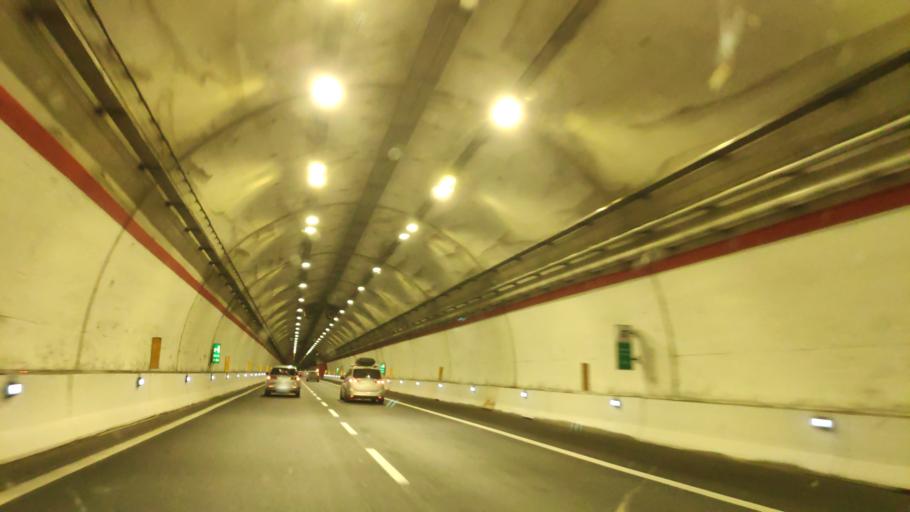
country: IT
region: Campania
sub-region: Provincia di Salerno
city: Petina
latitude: 40.5662
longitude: 15.3729
